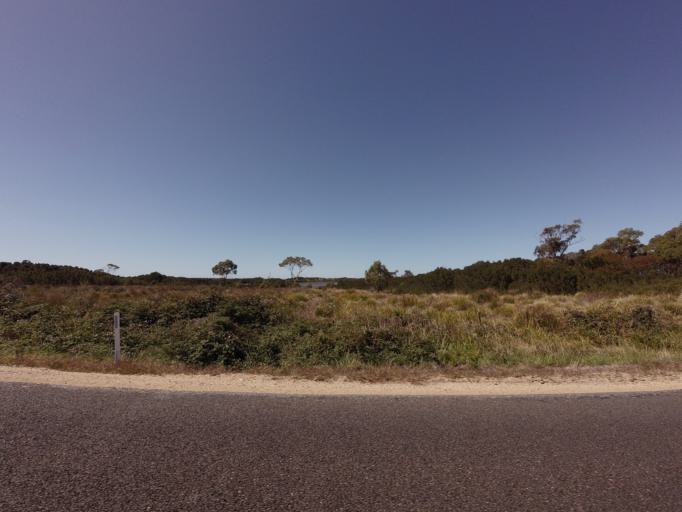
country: AU
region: Tasmania
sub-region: Break O'Day
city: St Helens
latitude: -41.7212
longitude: 148.2737
